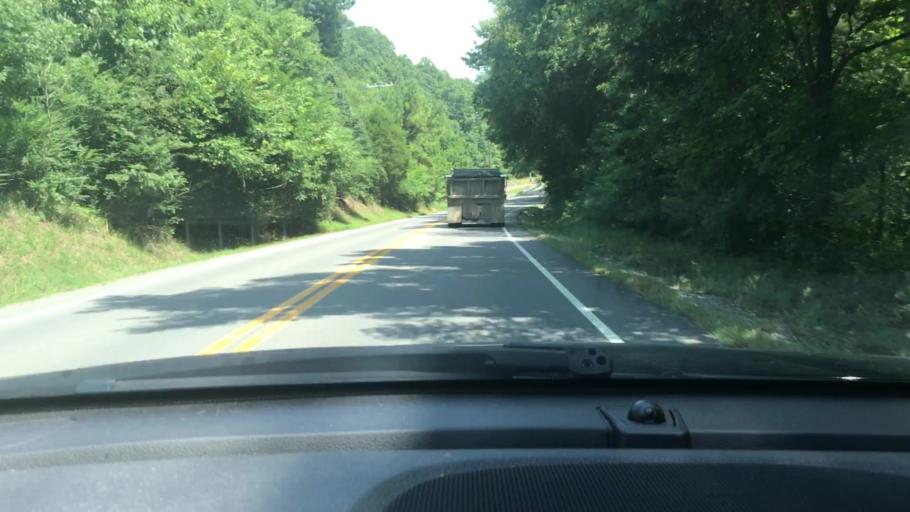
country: US
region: Tennessee
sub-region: Sumner County
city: Shackle Island
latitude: 36.4131
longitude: -86.6432
